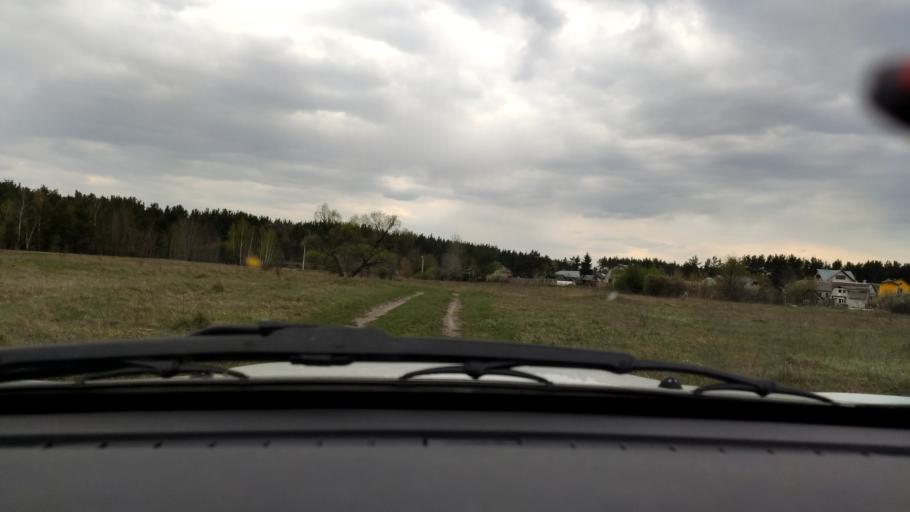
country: RU
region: Voronezj
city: Somovo
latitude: 51.7362
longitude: 39.3383
